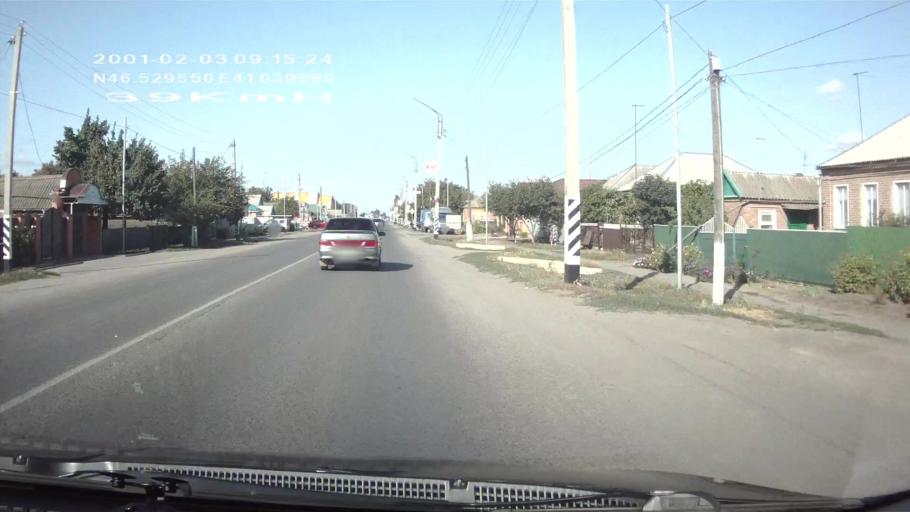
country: RU
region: Rostov
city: Tselina
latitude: 46.5295
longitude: 41.0394
